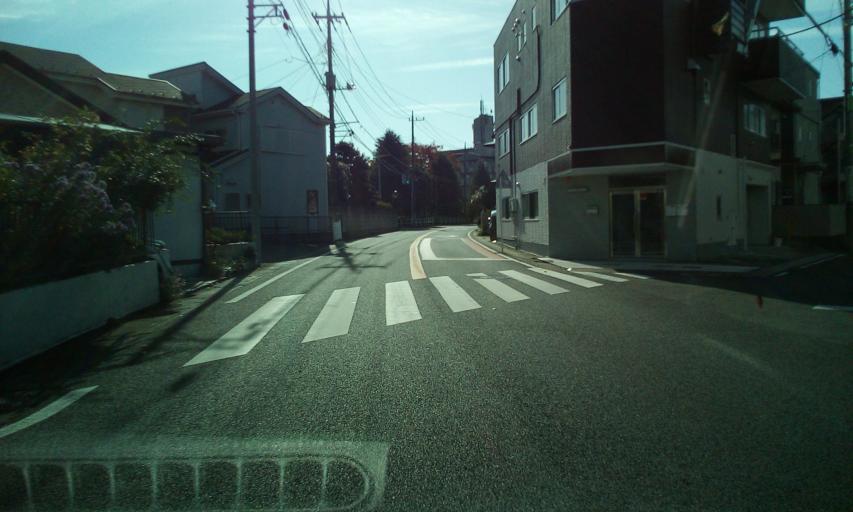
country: JP
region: Chiba
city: Nagareyama
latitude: 35.8579
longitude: 139.8898
